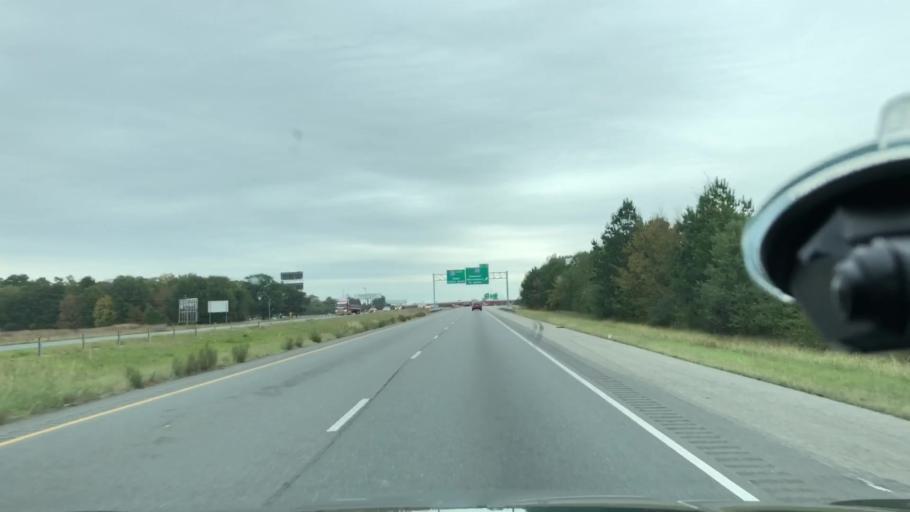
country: US
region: Arkansas
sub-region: Miller County
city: Texarkana
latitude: 33.4773
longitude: -93.9990
